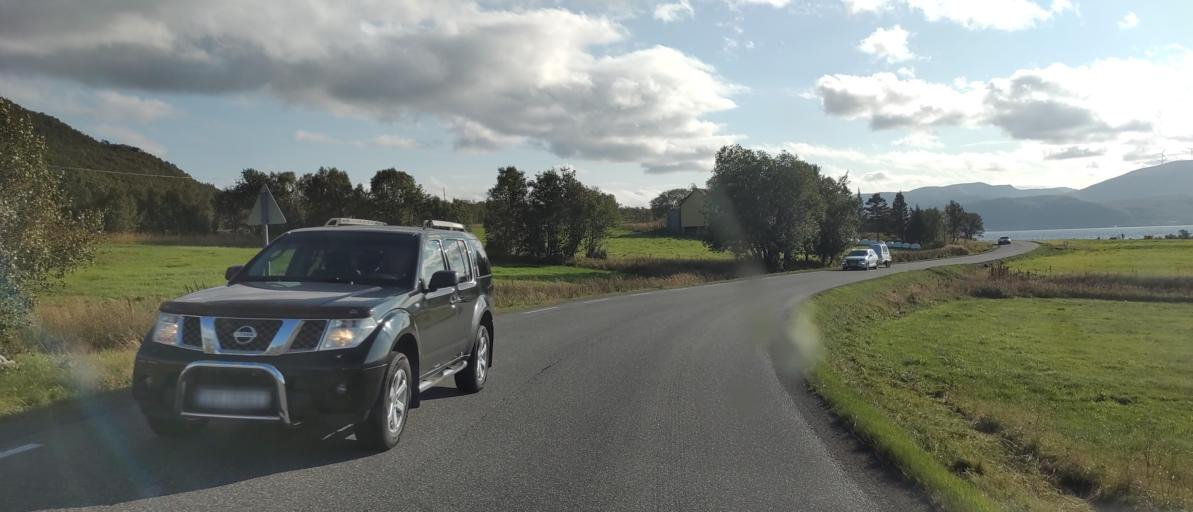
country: NO
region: Nordland
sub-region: Sortland
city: Sortland
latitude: 68.7675
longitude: 15.4671
